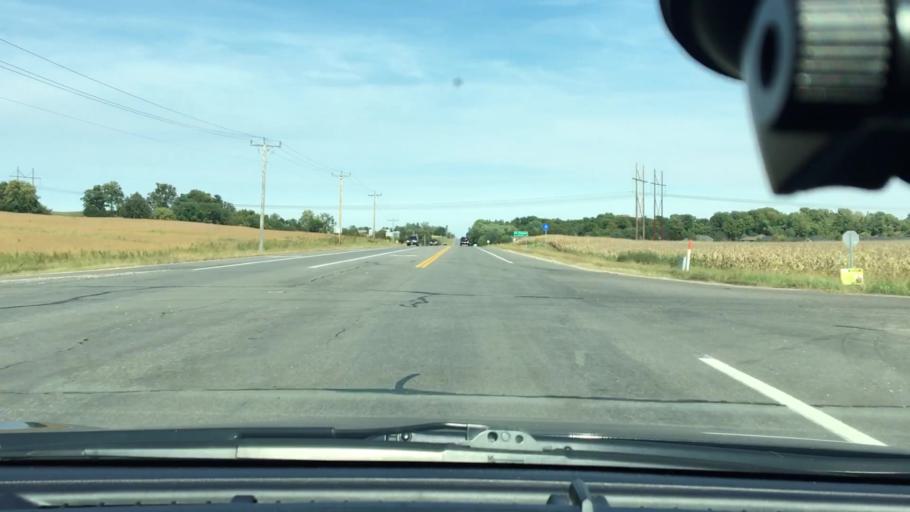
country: US
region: Minnesota
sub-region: Wright County
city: Hanover
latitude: 45.1740
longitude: -93.6656
